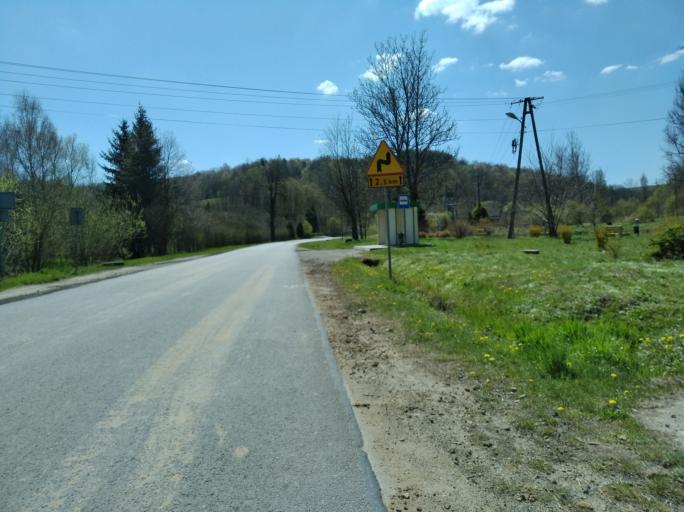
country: PL
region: Subcarpathian Voivodeship
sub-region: Powiat brzozowski
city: Dydnia
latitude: 49.6978
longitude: 22.1923
